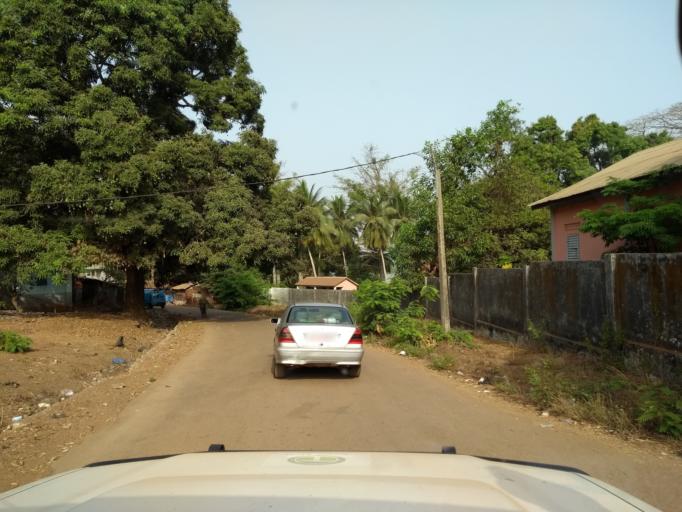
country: GN
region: Kindia
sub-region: Prefecture de Dubreka
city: Dubreka
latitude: 9.7928
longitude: -13.5239
